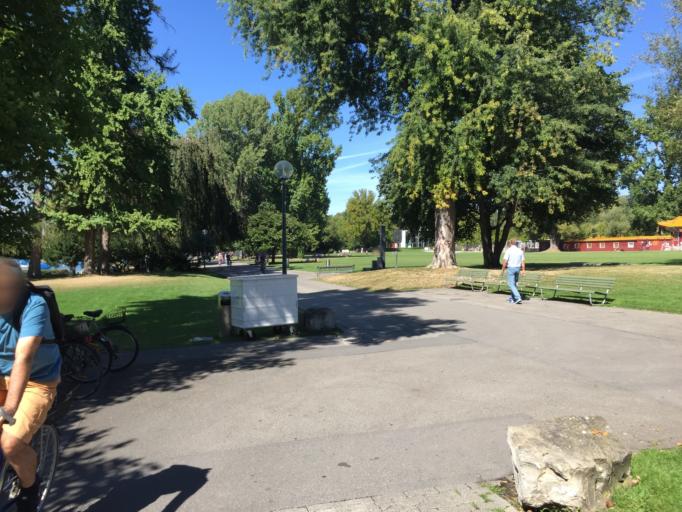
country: CH
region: Zurich
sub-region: Bezirk Zuerich
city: Zuerich (Kreis 8) / Seefeld
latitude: 47.3537
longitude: 8.5513
